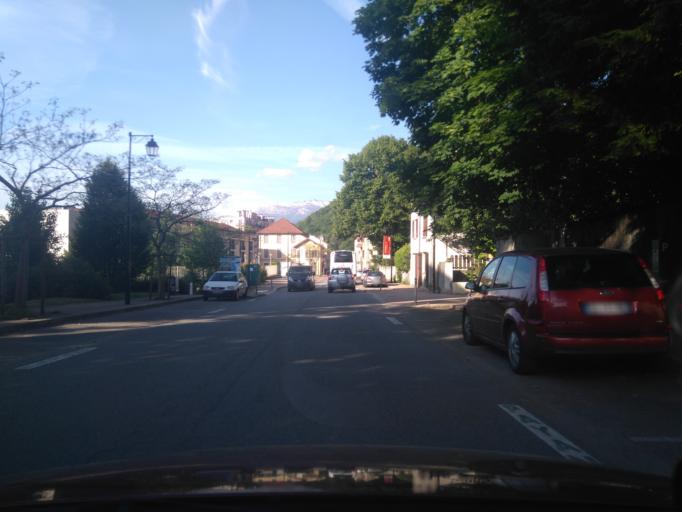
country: FR
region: Rhone-Alpes
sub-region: Departement de l'Isere
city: La Tronche
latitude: 45.2043
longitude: 5.7374
